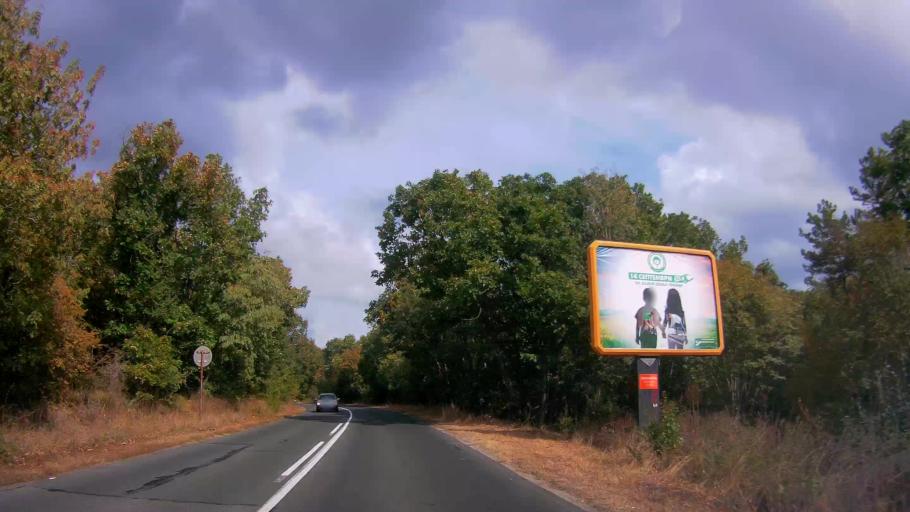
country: BG
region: Burgas
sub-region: Obshtina Primorsko
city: Primorsko
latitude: 42.2908
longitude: 27.7345
